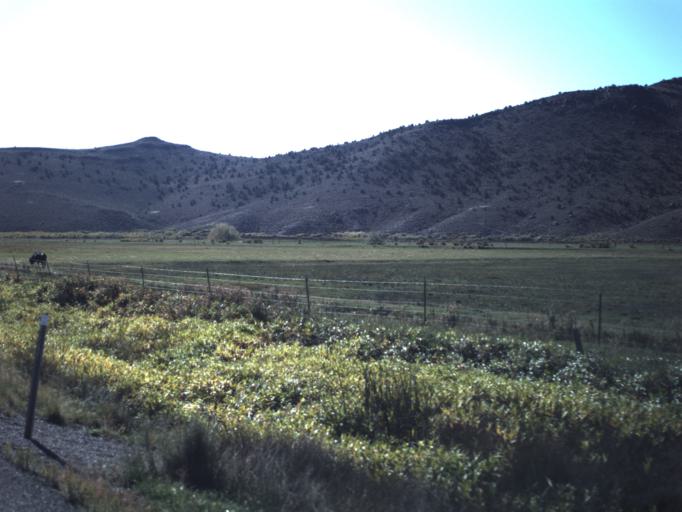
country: US
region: Utah
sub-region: Piute County
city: Junction
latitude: 38.1671
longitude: -112.0386
